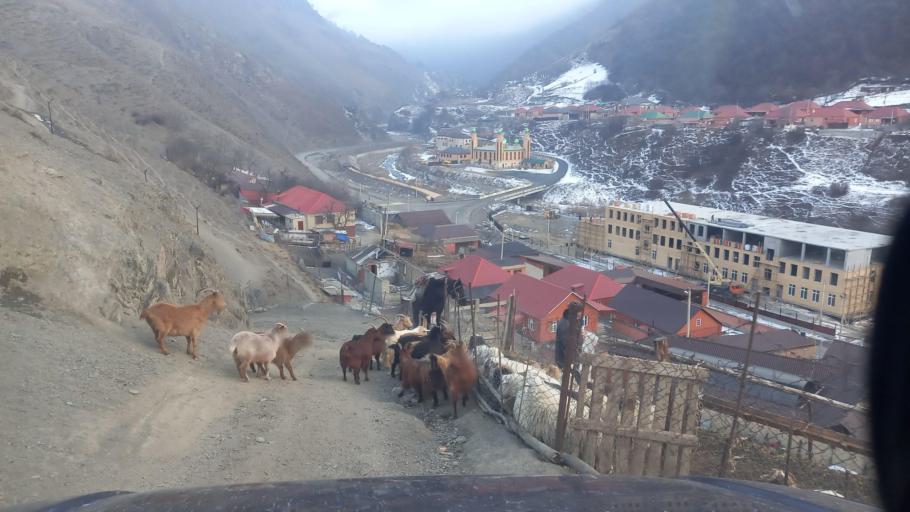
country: RU
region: Ingushetiya
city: Dzhayrakh
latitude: 42.8035
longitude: 44.7542
